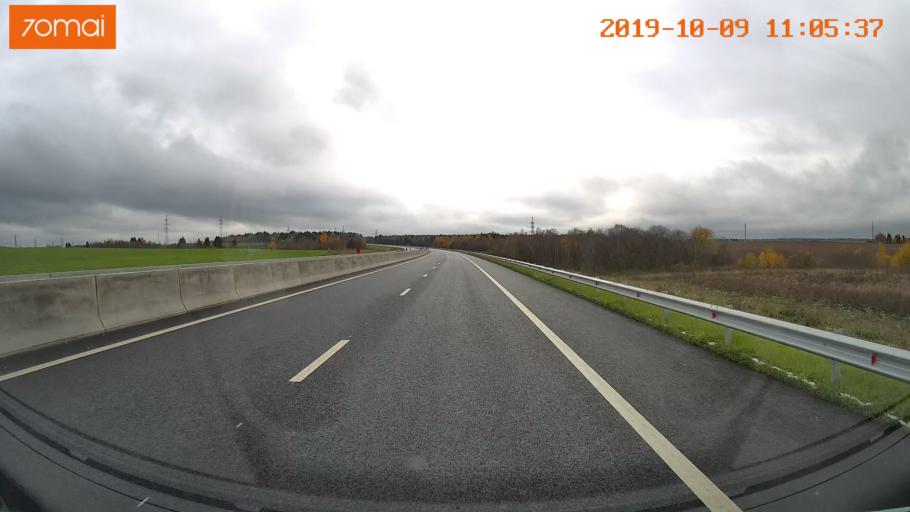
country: RU
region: Vologda
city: Molochnoye
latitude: 59.1976
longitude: 39.7581
